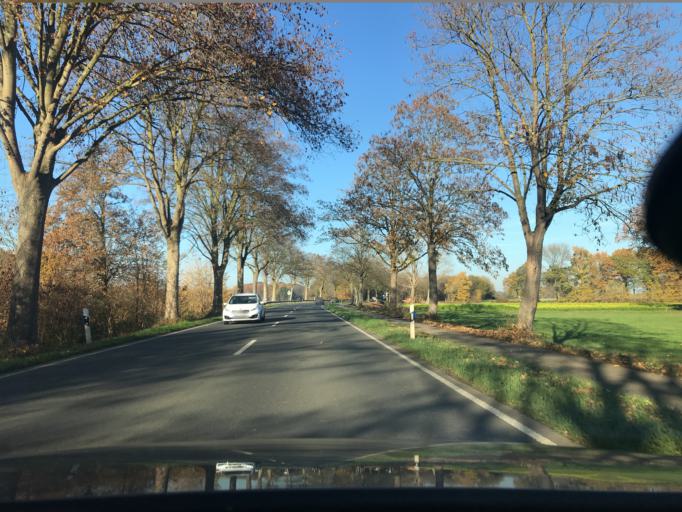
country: DE
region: North Rhine-Westphalia
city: Kempen
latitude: 51.4164
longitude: 6.4177
